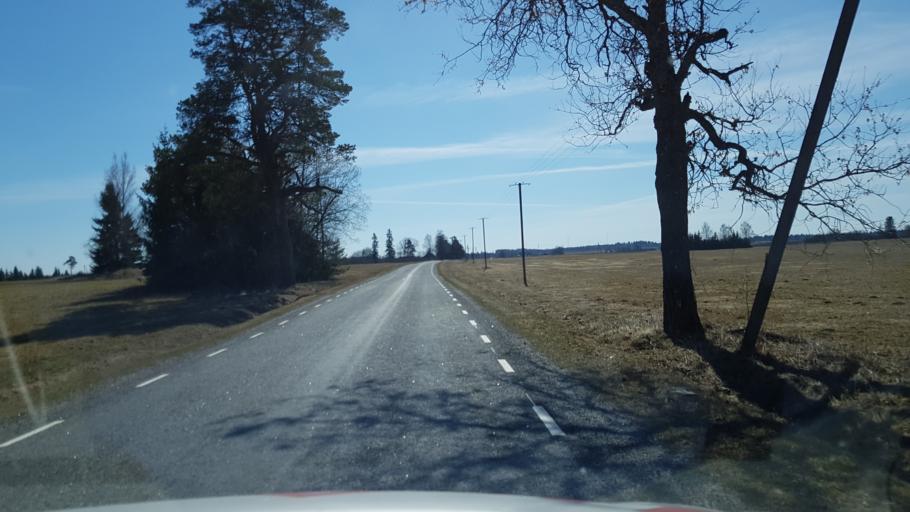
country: EE
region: Laeaene-Virumaa
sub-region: Vinni vald
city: Vinni
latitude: 59.1233
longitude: 26.5219
